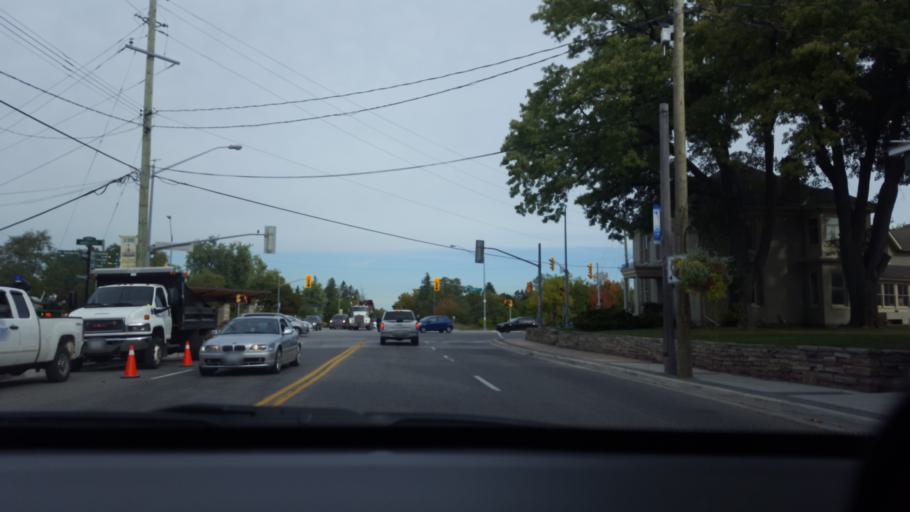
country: CA
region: Ontario
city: Vaughan
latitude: 43.9282
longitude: -79.5281
